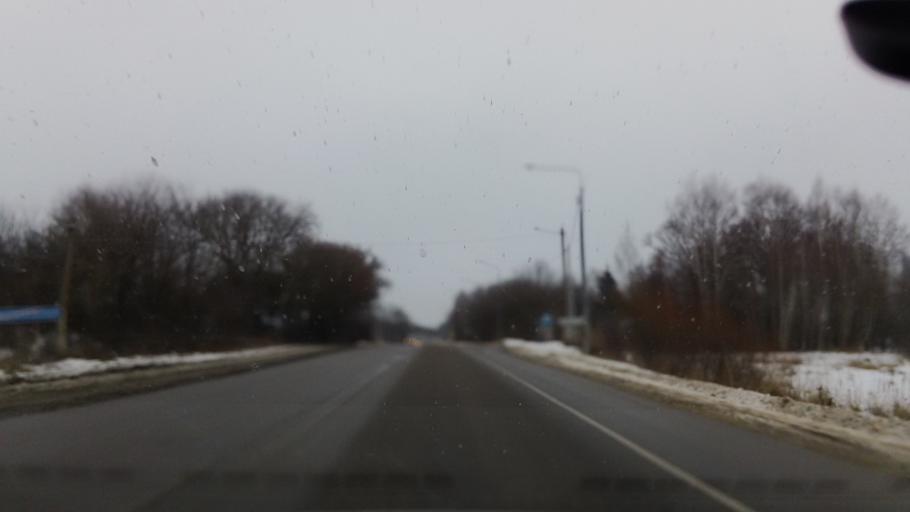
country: RU
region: Tula
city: Bolokhovo
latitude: 54.0532
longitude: 37.8119
